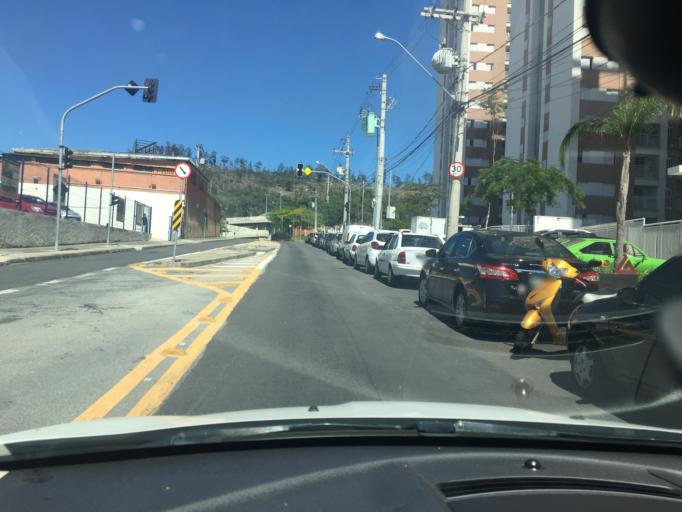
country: BR
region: Sao Paulo
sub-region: Jundiai
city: Jundiai
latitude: -23.2117
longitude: -46.8869
